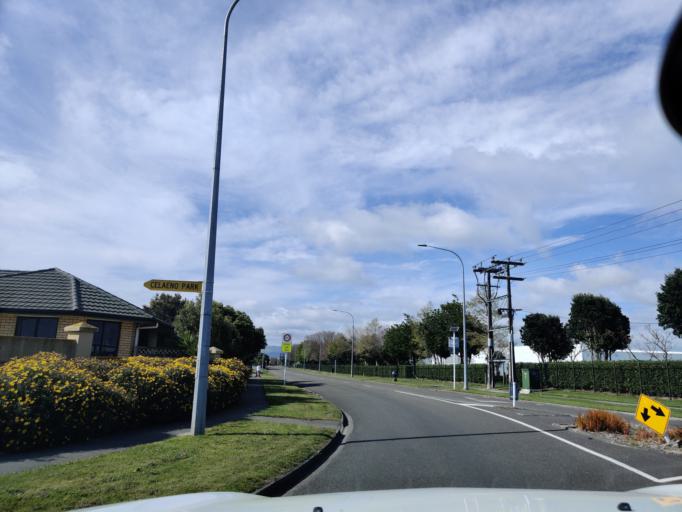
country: NZ
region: Manawatu-Wanganui
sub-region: Palmerston North City
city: Palmerston North
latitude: -40.3306
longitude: 175.6524
